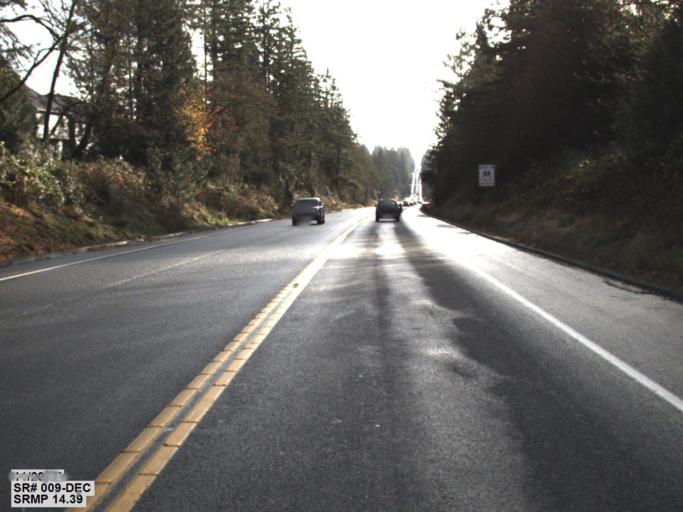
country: US
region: Washington
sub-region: Snohomish County
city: West Lake Stevens
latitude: 47.9832
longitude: -122.1031
